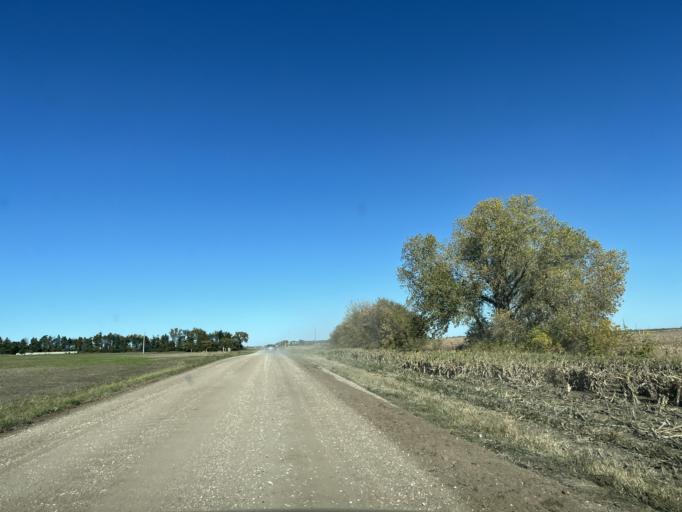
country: US
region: Kansas
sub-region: McPherson County
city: Moundridge
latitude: 38.2157
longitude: -97.6292
